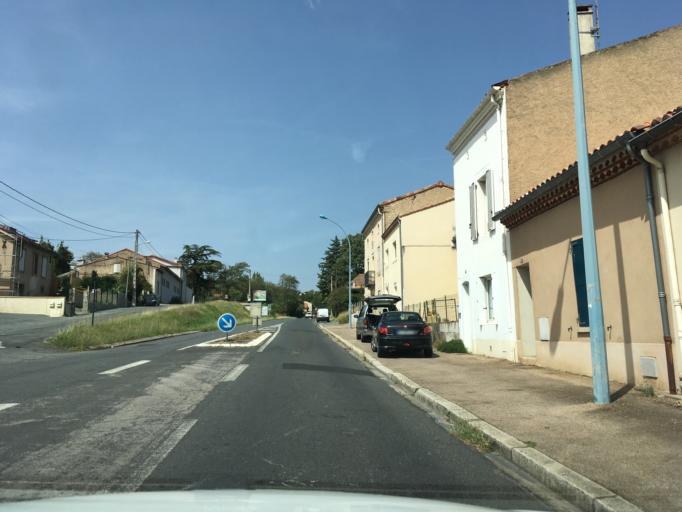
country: FR
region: Midi-Pyrenees
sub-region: Departement du Tarn
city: Castres
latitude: 43.6097
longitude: 2.2284
